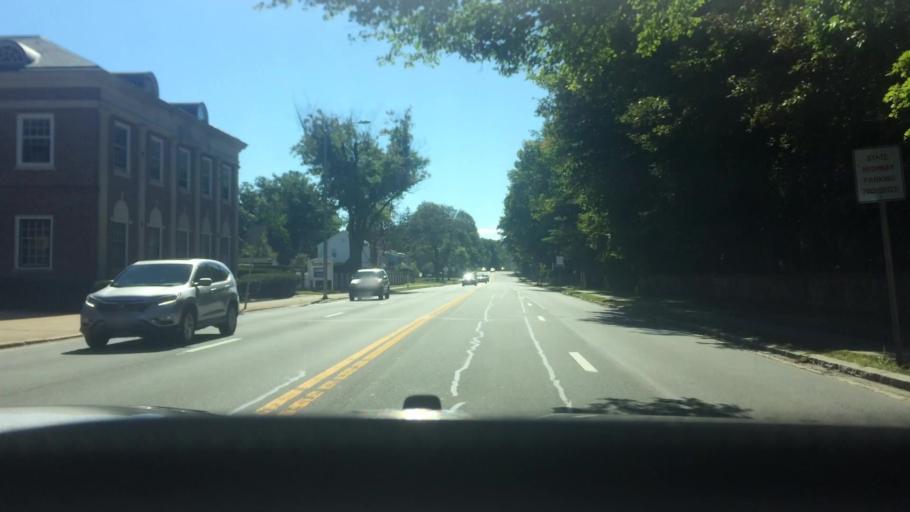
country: US
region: Massachusetts
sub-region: Essex County
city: Andover
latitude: 42.6711
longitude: -71.1501
